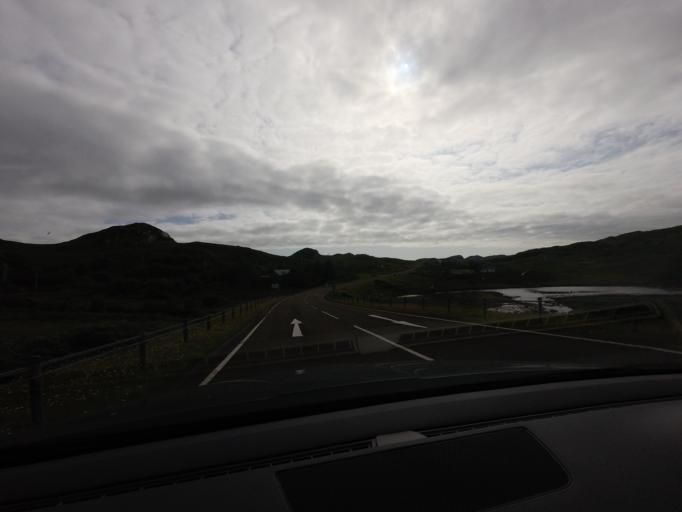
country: GB
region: Scotland
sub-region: Highland
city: Ullapool
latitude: 58.4237
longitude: -4.9907
